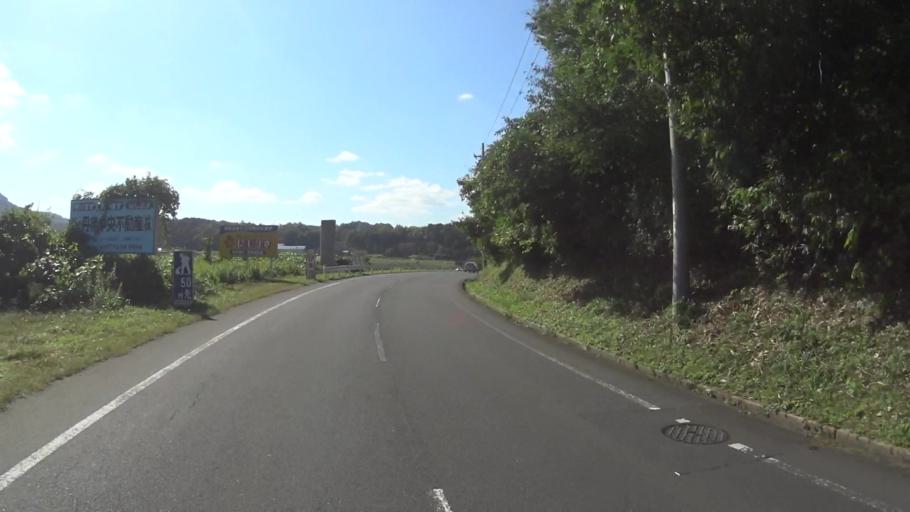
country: JP
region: Kyoto
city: Miyazu
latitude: 35.6447
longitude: 135.0844
